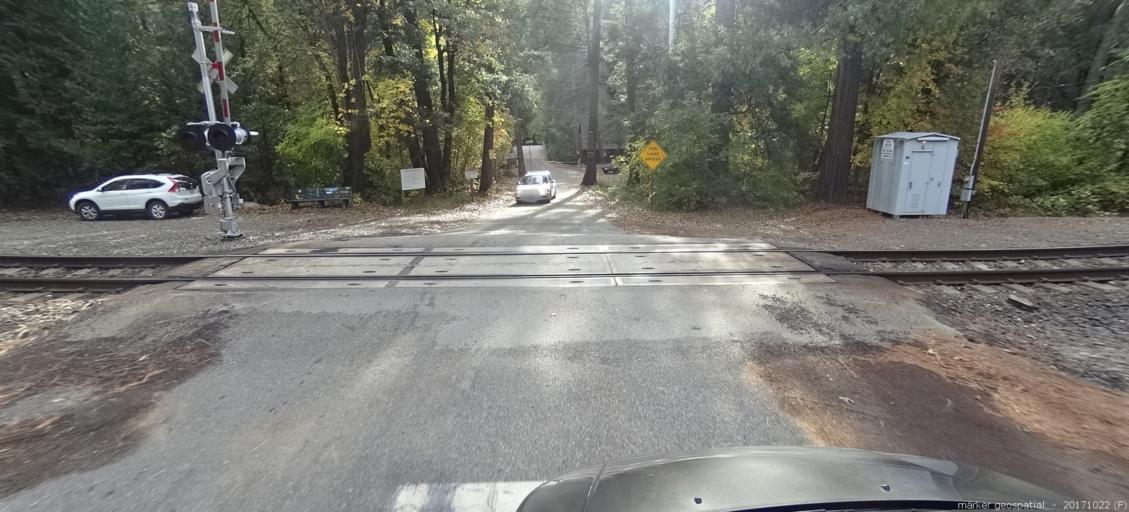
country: US
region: California
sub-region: Siskiyou County
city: Dunsmuir
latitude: 41.1304
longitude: -122.3208
